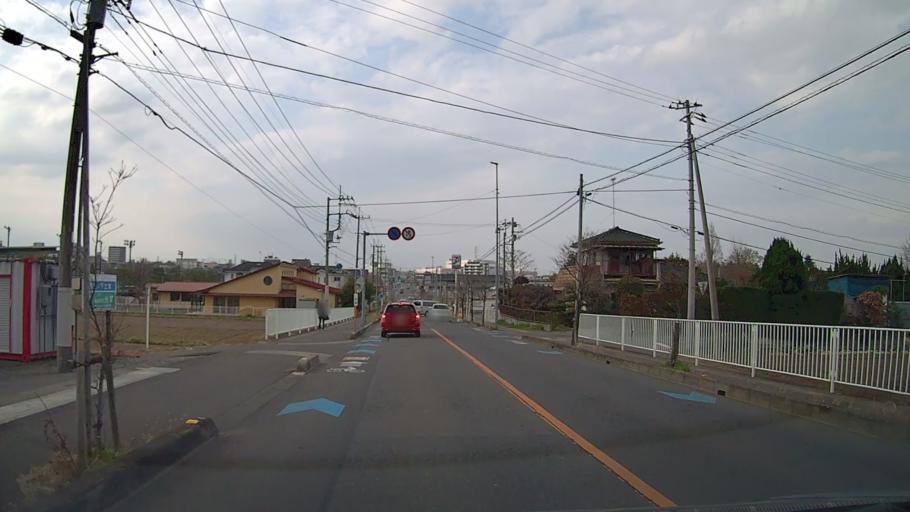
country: JP
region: Saitama
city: Asaka
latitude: 35.8135
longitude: 139.5974
